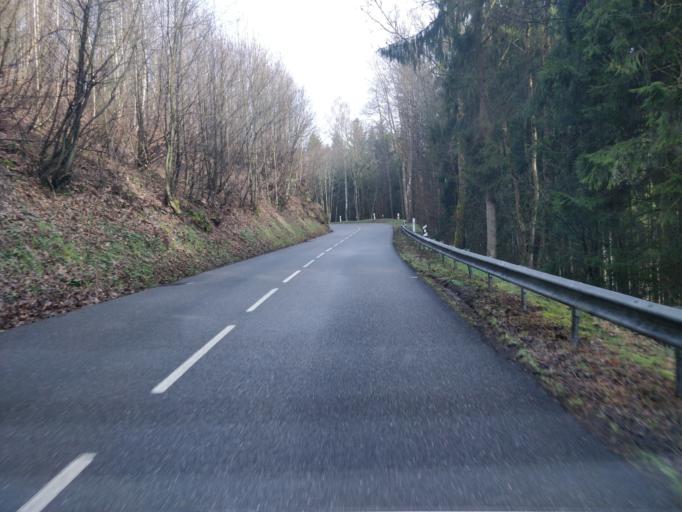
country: FR
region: Lorraine
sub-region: Departement de la Moselle
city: Soucht
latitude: 48.9166
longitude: 7.3249
